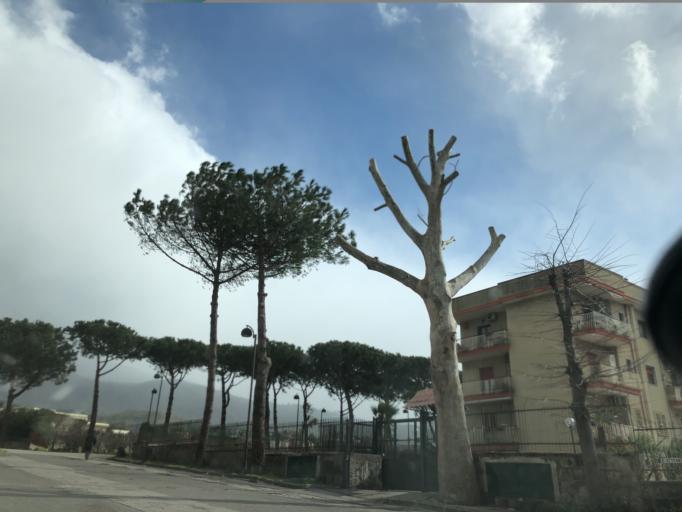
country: IT
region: Campania
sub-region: Provincia di Napoli
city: San Sebastiano al Vesuvio
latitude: 40.8410
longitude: 14.3620
